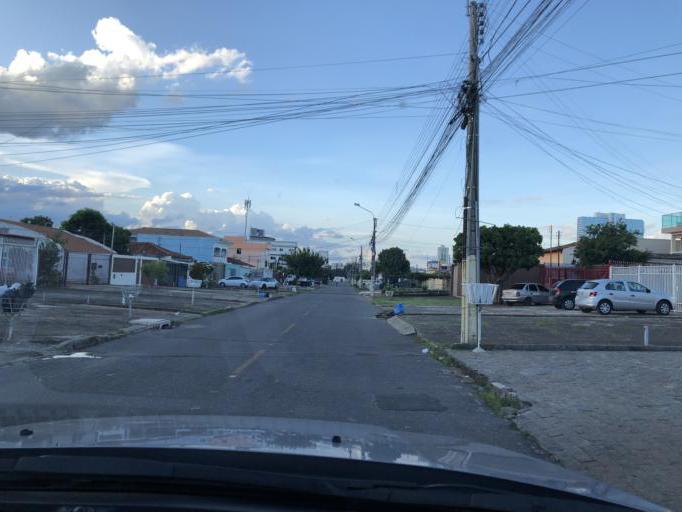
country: BR
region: Federal District
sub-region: Brasilia
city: Brasilia
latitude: -15.8478
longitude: -48.0448
